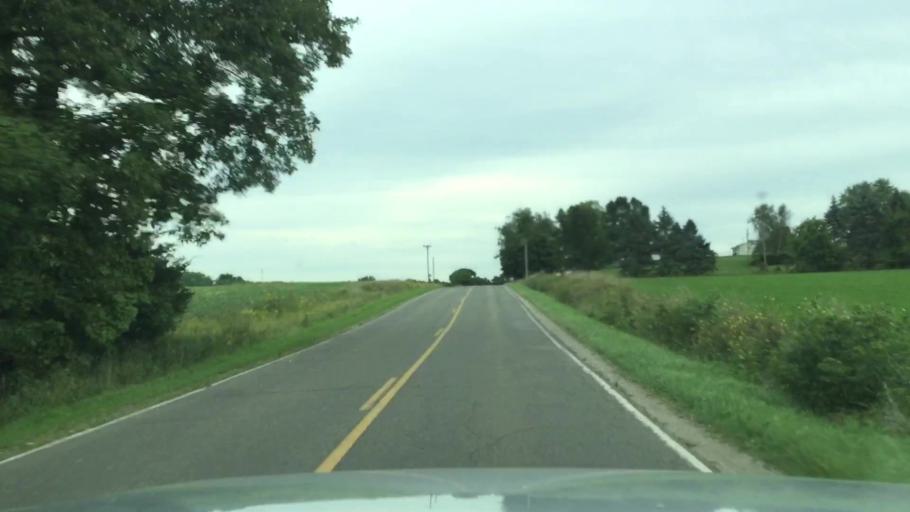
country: US
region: Michigan
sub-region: Shiawassee County
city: Durand
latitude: 42.8583
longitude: -84.0408
